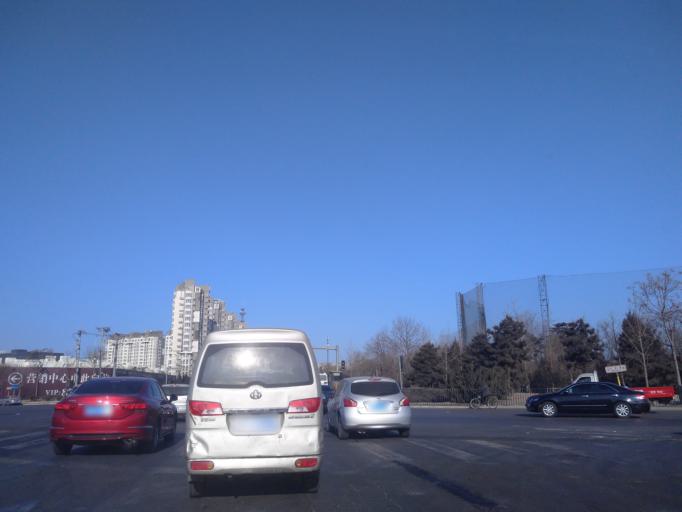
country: CN
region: Beijing
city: Jiugong
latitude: 39.8238
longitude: 116.4753
